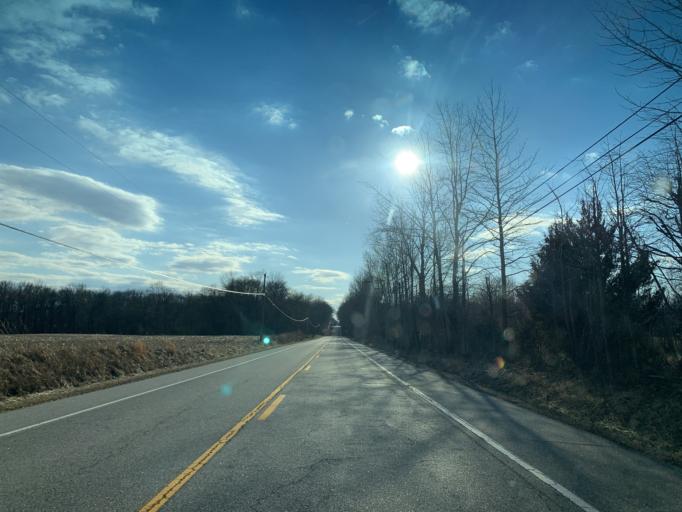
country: US
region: Maryland
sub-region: Queen Anne's County
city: Kingstown
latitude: 39.1625
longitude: -75.9404
